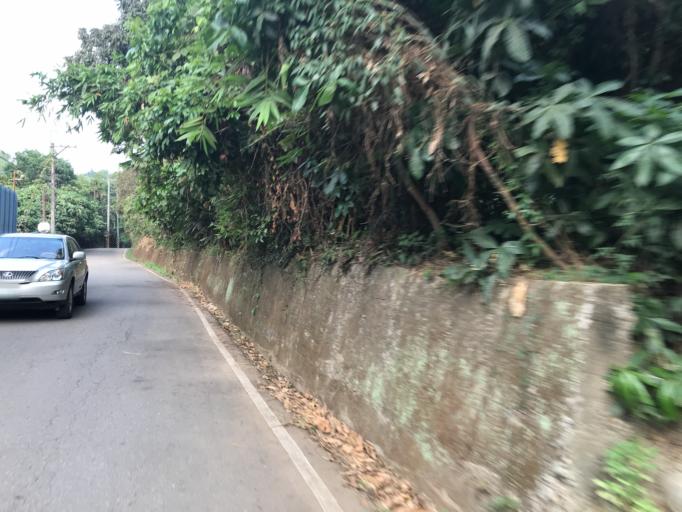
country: TW
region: Taiwan
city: Zhongxing New Village
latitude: 24.0406
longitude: 120.7044
